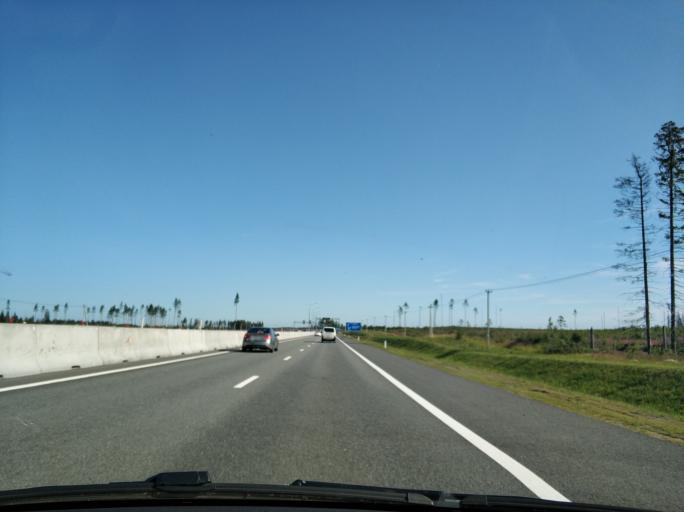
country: RU
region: Leningrad
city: Sosnovo
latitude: 60.4949
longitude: 30.1958
